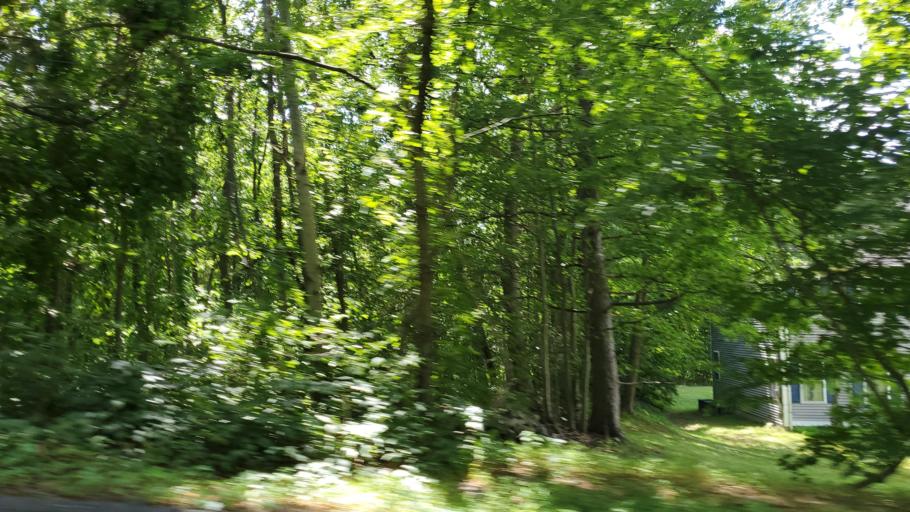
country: US
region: Connecticut
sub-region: Fairfield County
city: Newtown
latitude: 41.3542
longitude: -73.2771
